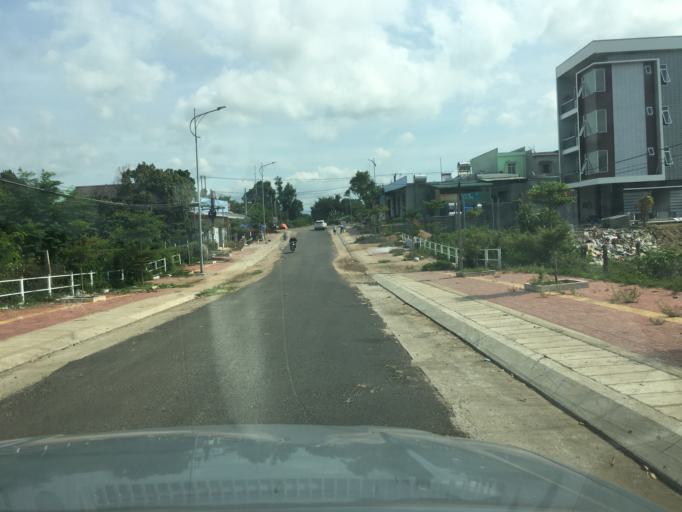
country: VN
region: Gia Lai
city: Kong Chro
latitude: 13.7758
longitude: 108.5219
